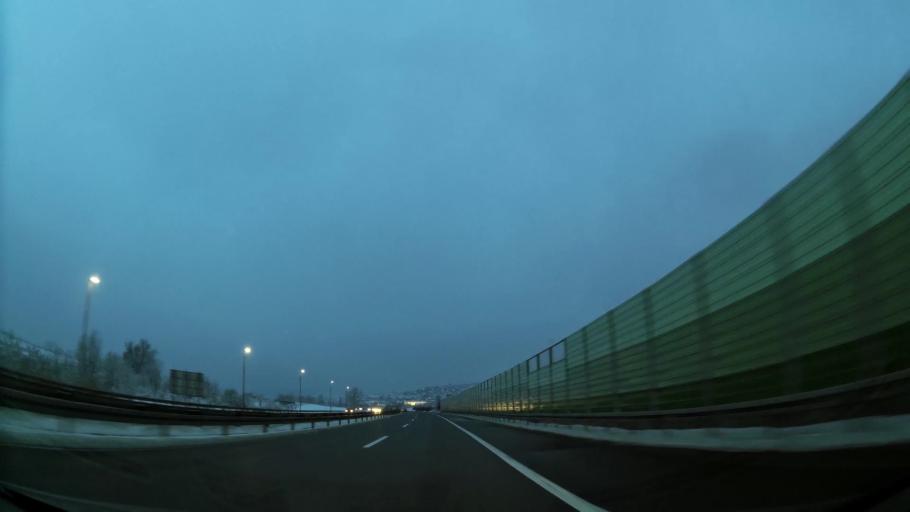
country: RS
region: Central Serbia
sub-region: Belgrade
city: Zvezdara
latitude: 44.6949
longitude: 20.5834
